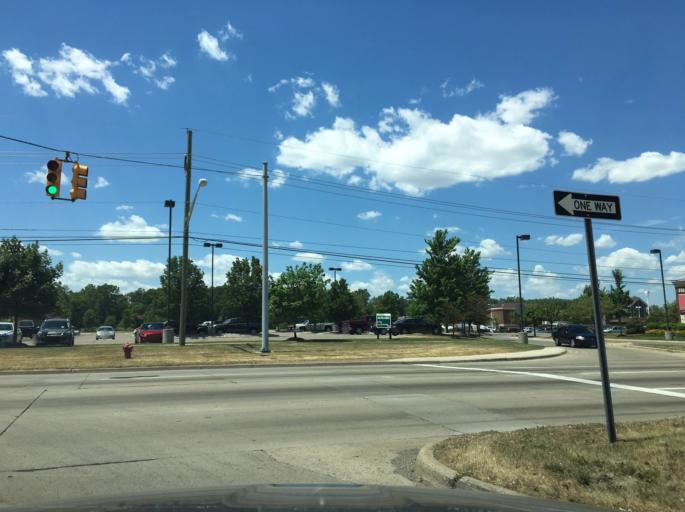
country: US
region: Michigan
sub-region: Macomb County
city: Center Line
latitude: 42.5081
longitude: -83.0466
